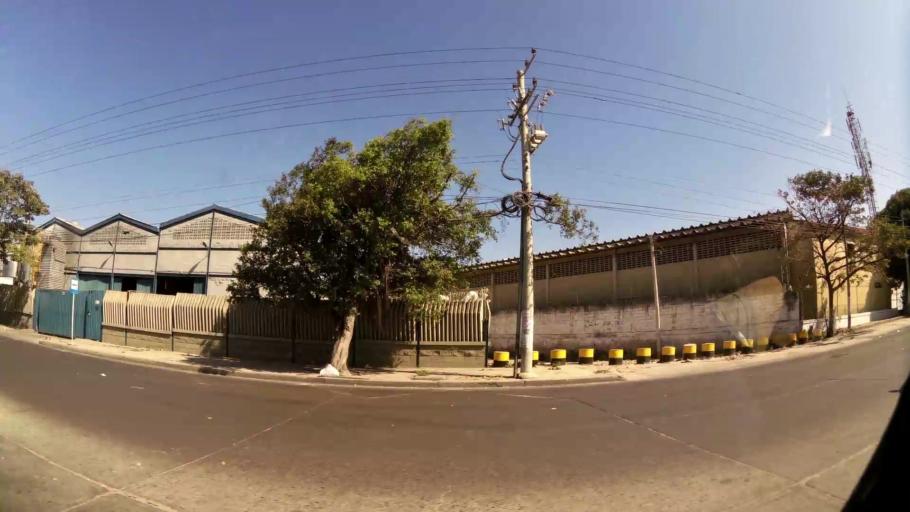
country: CO
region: Atlantico
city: Barranquilla
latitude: 10.9610
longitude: -74.7845
